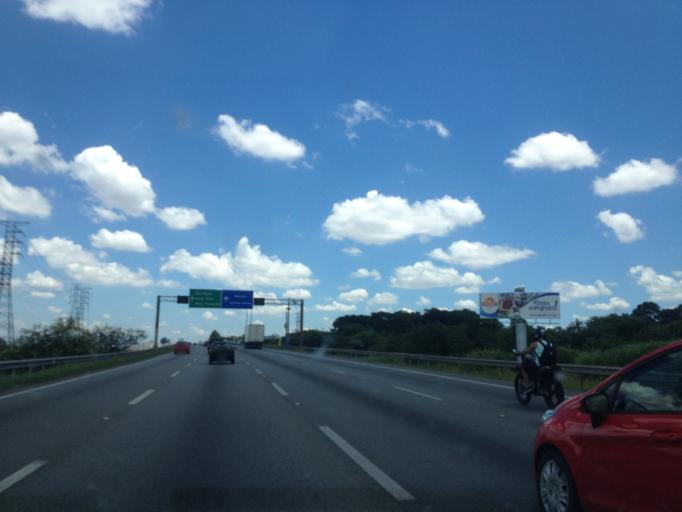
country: BR
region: Sao Paulo
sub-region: Guarulhos
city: Guarulhos
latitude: -23.4750
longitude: -46.5131
